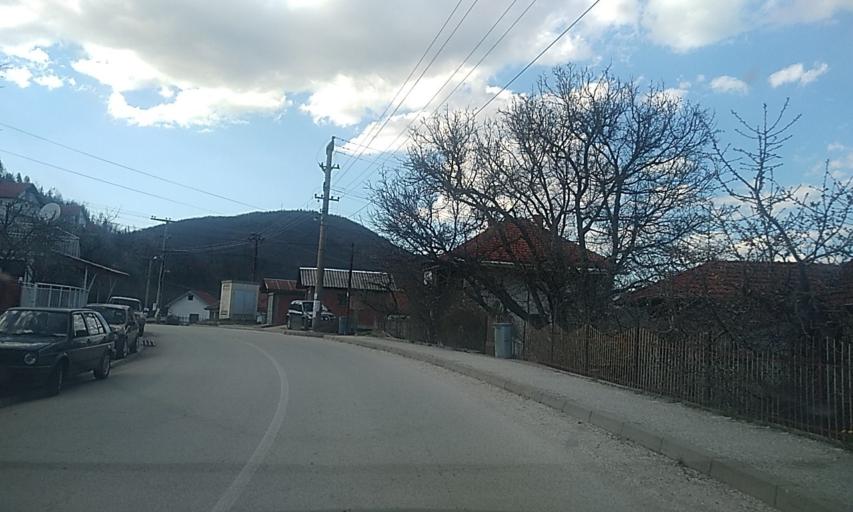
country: RS
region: Central Serbia
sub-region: Pcinjski Okrug
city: Bosilegrad
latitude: 42.4895
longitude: 22.4718
